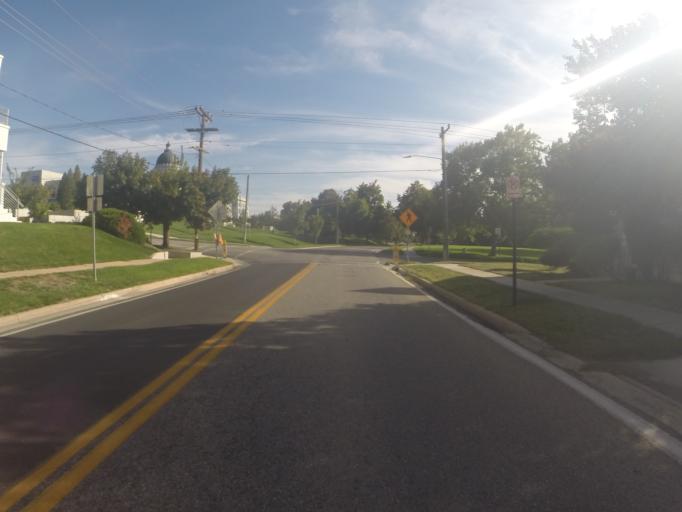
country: US
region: Utah
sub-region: Salt Lake County
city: Salt Lake City
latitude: 40.7804
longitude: -111.8900
